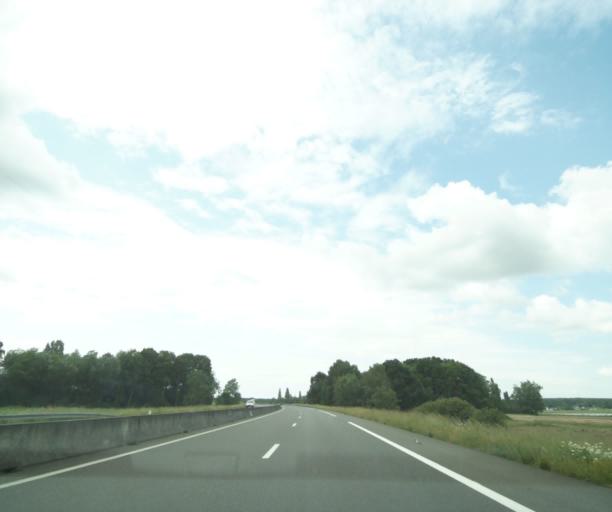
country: FR
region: Pays de la Loire
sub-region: Departement de Maine-et-Loire
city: Vivy
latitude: 47.3294
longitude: -0.0362
